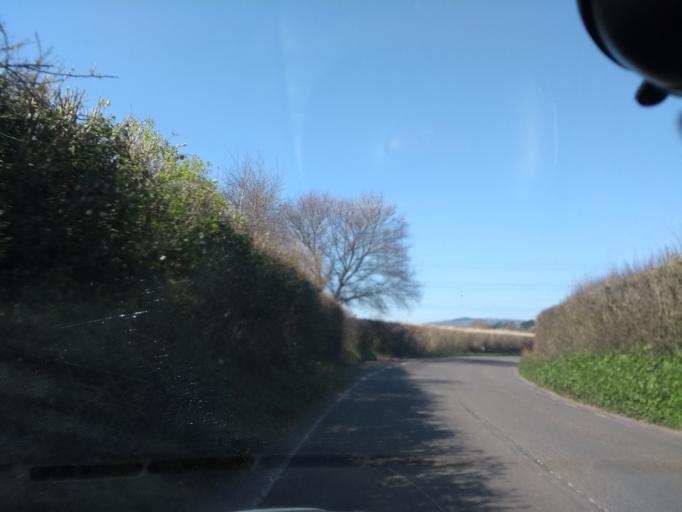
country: GB
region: England
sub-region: Somerset
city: Taunton
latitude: 51.0449
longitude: -3.1117
